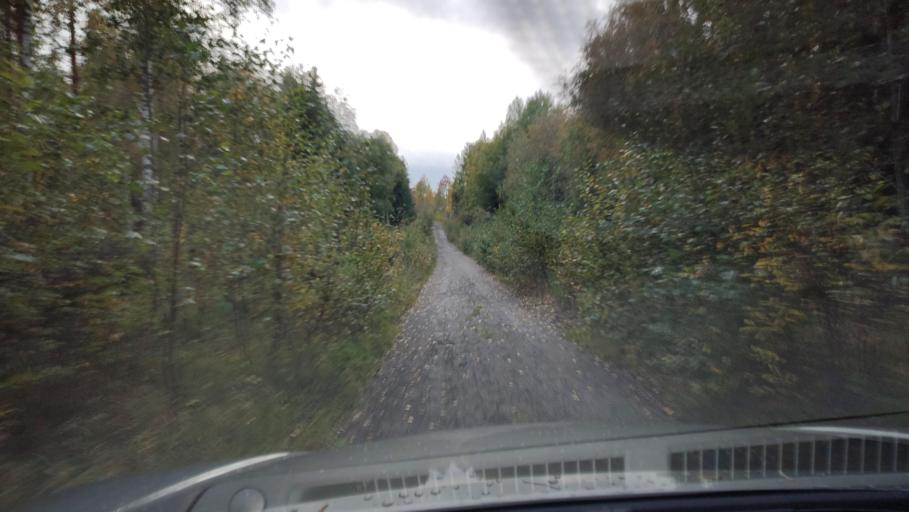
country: FI
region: Ostrobothnia
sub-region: Sydosterbotten
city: Kristinestad
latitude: 62.2725
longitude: 21.4422
